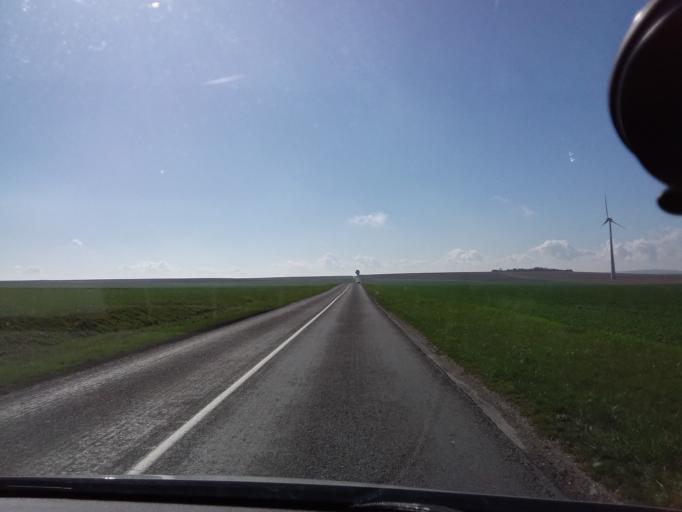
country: FR
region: Picardie
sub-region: Departement de l'Aisne
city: Guignicourt
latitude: 49.5198
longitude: 4.0430
